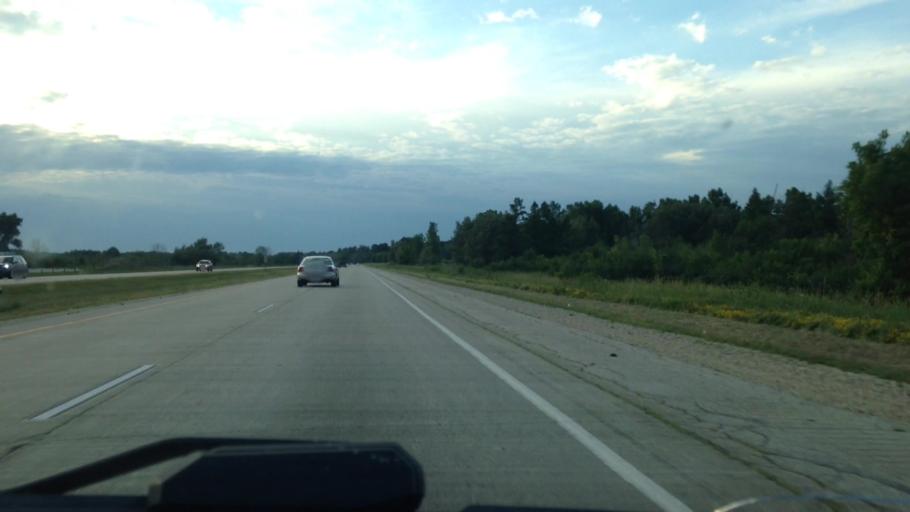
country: US
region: Wisconsin
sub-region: Washington County
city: Slinger
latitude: 43.3818
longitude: -88.3061
